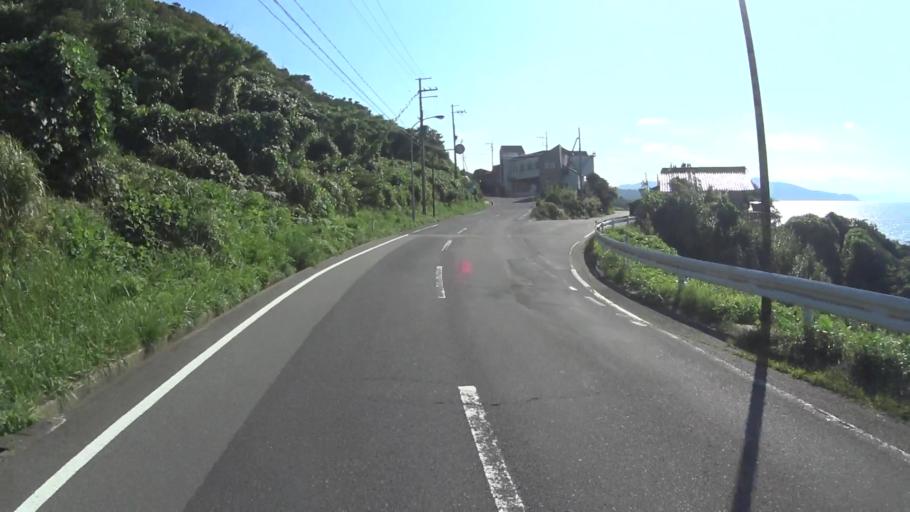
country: JP
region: Kyoto
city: Miyazu
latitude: 35.7165
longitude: 135.0685
